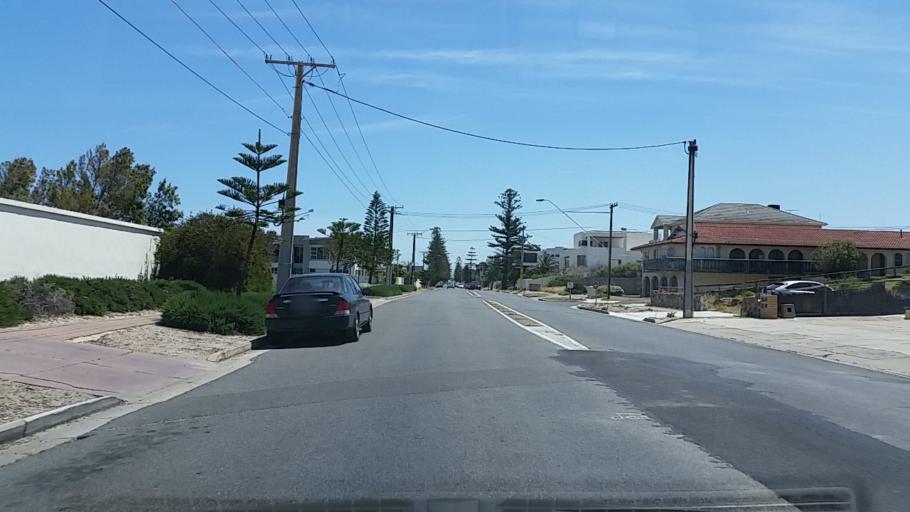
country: AU
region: South Australia
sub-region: Charles Sturt
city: Henley Beach
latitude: -34.9347
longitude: 138.4989
